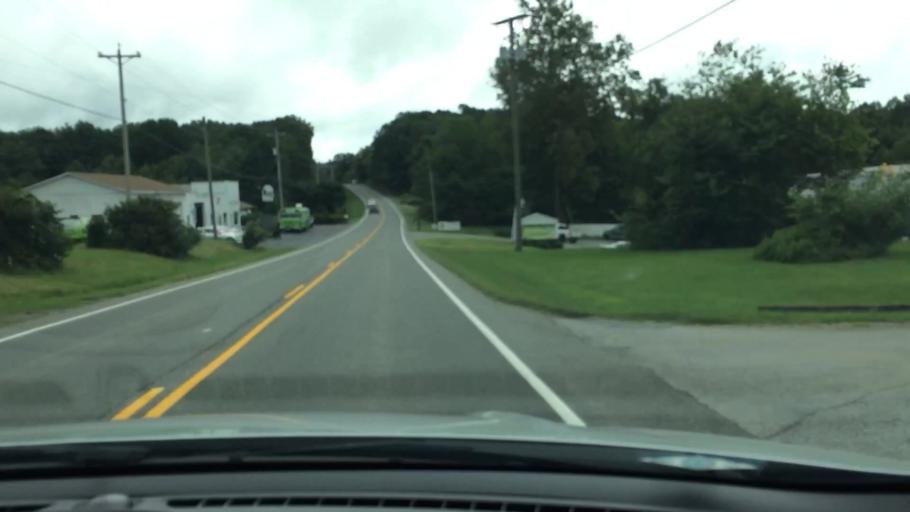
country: US
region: Virginia
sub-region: Franklin County
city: Union Hall
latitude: 37.0071
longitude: -79.7782
